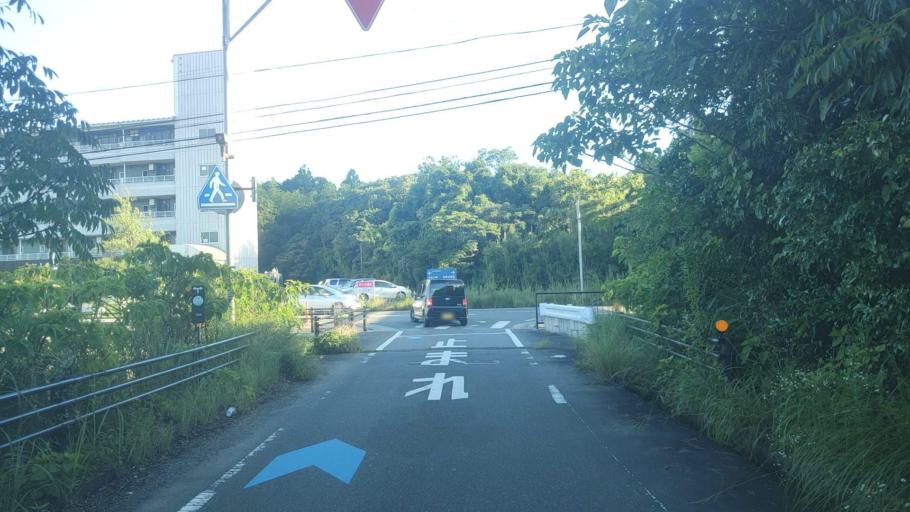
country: JP
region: Mie
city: Toba
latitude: 34.3315
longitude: 136.8405
